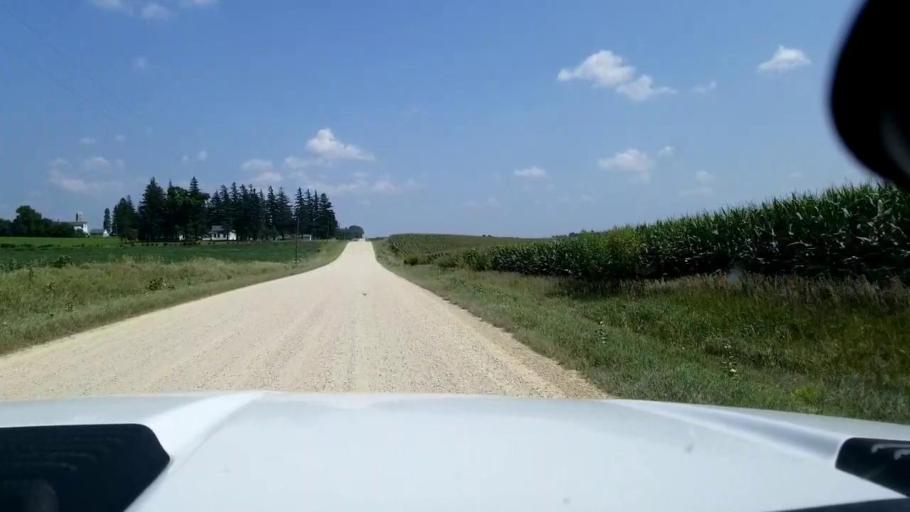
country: US
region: Minnesota
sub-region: Goodhue County
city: Wanamingo
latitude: 44.3416
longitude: -92.8895
